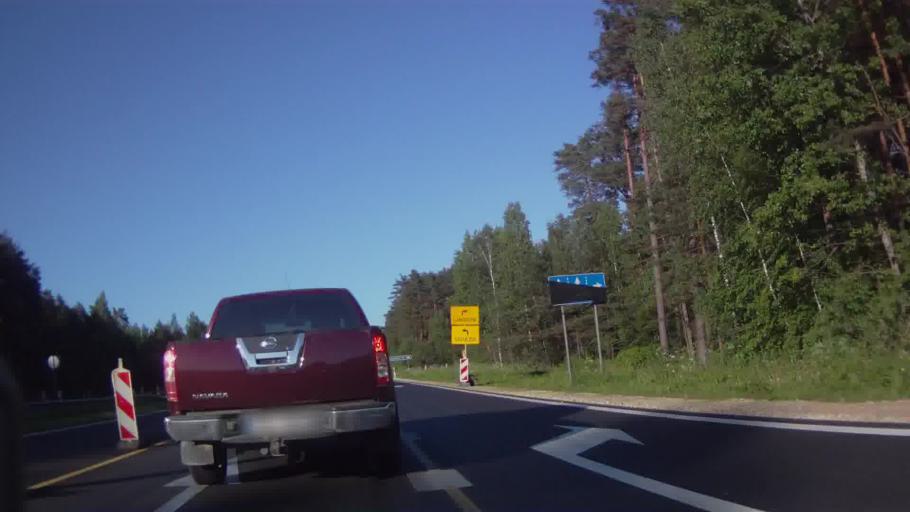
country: LV
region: Riga
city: Bergi
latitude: 57.0148
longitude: 24.3233
